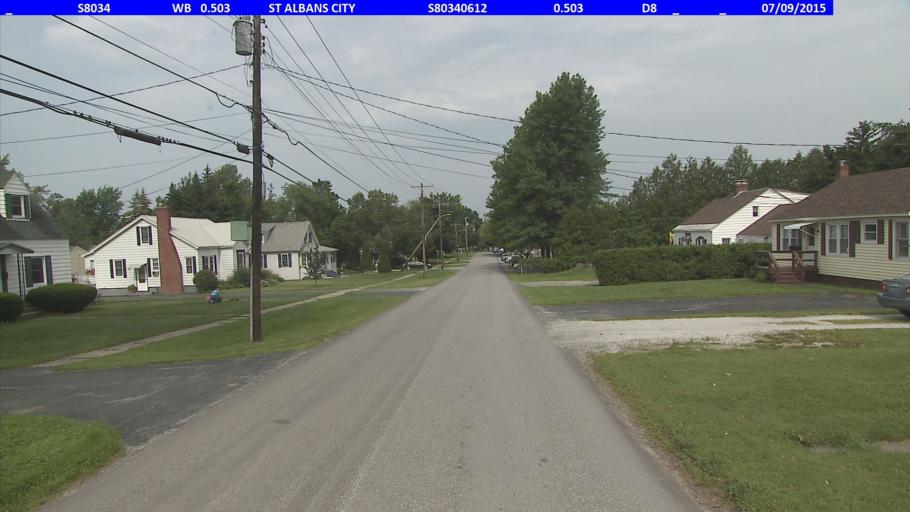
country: US
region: Vermont
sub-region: Franklin County
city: Saint Albans
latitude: 44.8040
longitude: -73.0759
